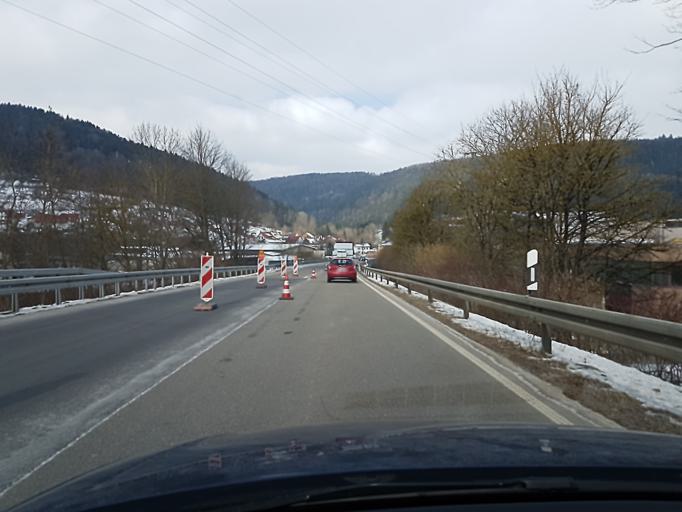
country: DE
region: Baden-Wuerttemberg
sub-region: Freiburg Region
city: Sulz am Neckar
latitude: 48.4177
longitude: 8.6370
